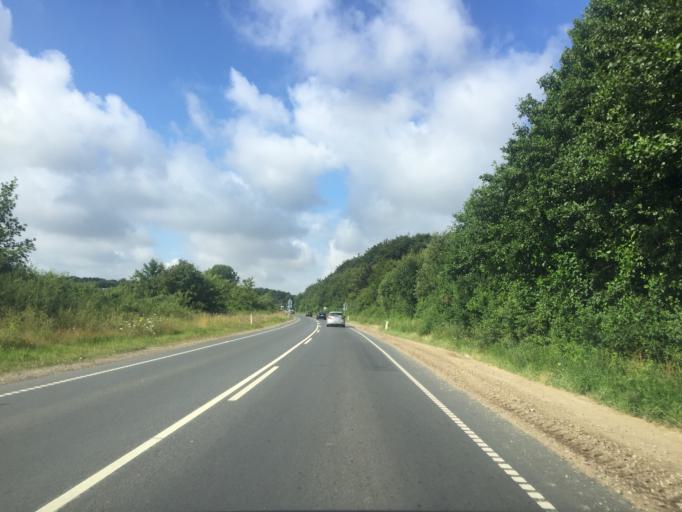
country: DK
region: South Denmark
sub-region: Svendborg Kommune
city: Svendborg
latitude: 55.0778
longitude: 10.6043
